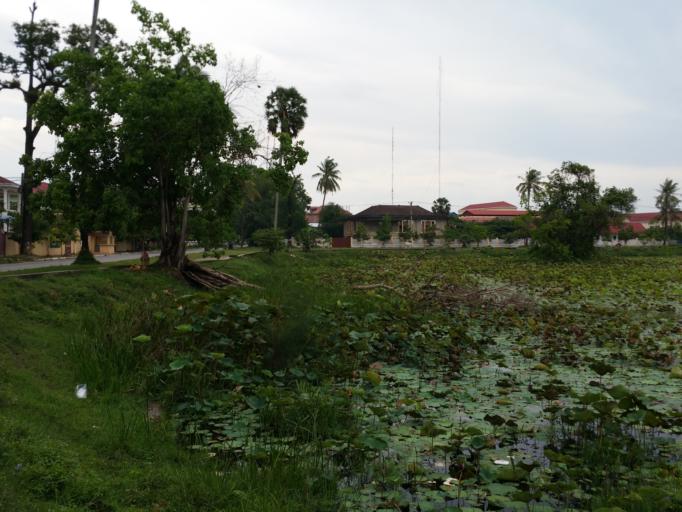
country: KH
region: Kampot
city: Kampot
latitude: 10.6029
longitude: 104.1815
